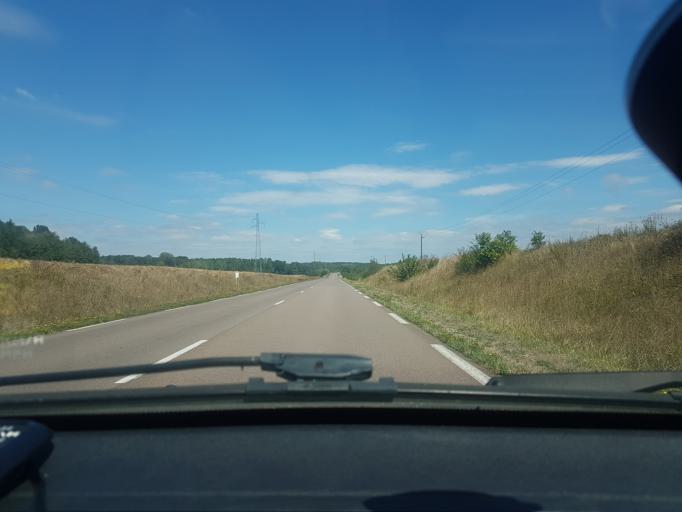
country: FR
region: Franche-Comte
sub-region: Departement de la Haute-Saone
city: Gray-la-Ville
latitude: 47.4227
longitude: 5.5243
